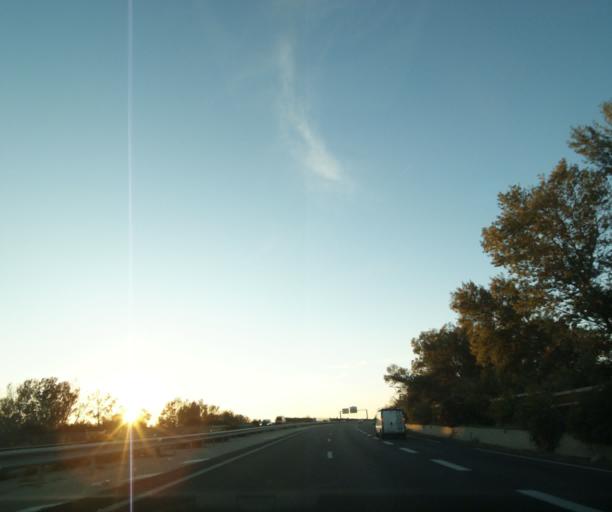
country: FR
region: Provence-Alpes-Cote d'Azur
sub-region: Departement des Bouches-du-Rhone
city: Salon-de-Provence
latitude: 43.6246
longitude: 5.0790
